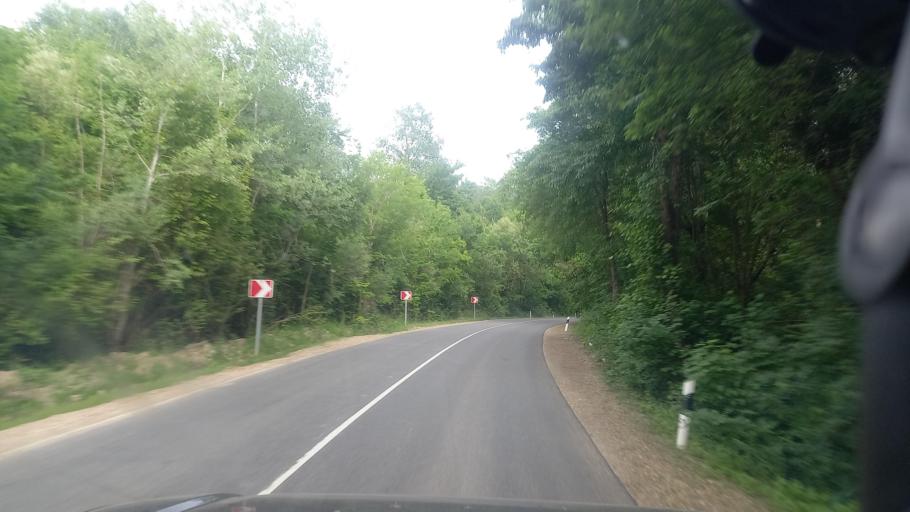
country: RU
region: Krasnodarskiy
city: Goryachiy Klyuch
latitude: 44.6017
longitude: 39.0435
